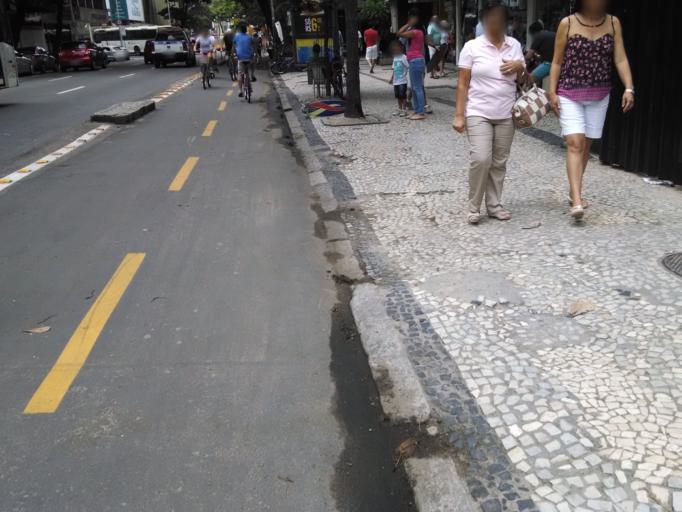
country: BR
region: Rio de Janeiro
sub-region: Rio De Janeiro
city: Rio de Janeiro
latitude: -22.9870
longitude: -43.1907
